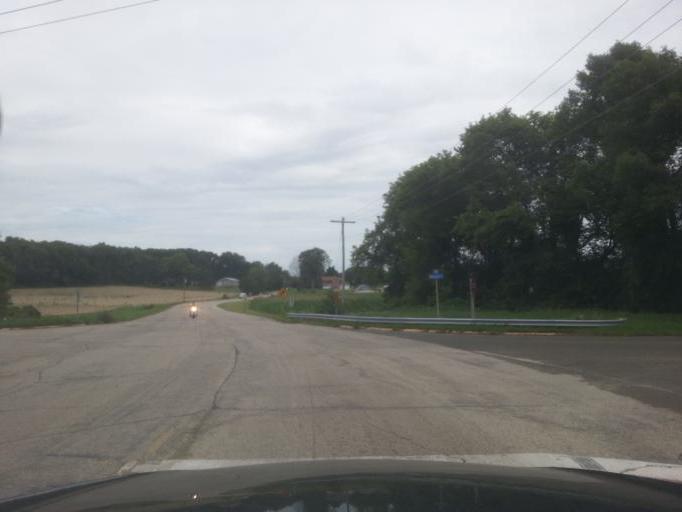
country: US
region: Wisconsin
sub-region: Dane County
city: Cottage Grove
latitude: 43.0513
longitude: -89.2462
